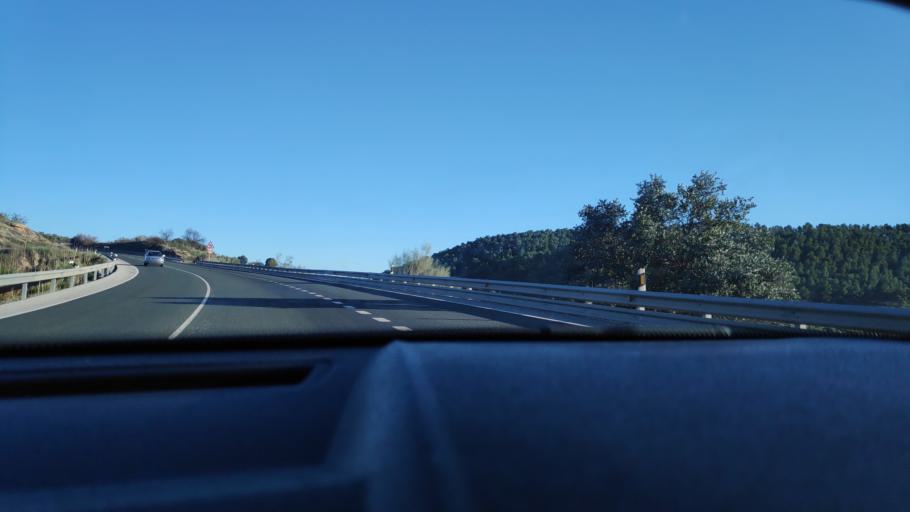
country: ES
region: Andalusia
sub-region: Province of Cordoba
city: Fuente-Tojar
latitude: 37.5759
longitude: -4.1572
